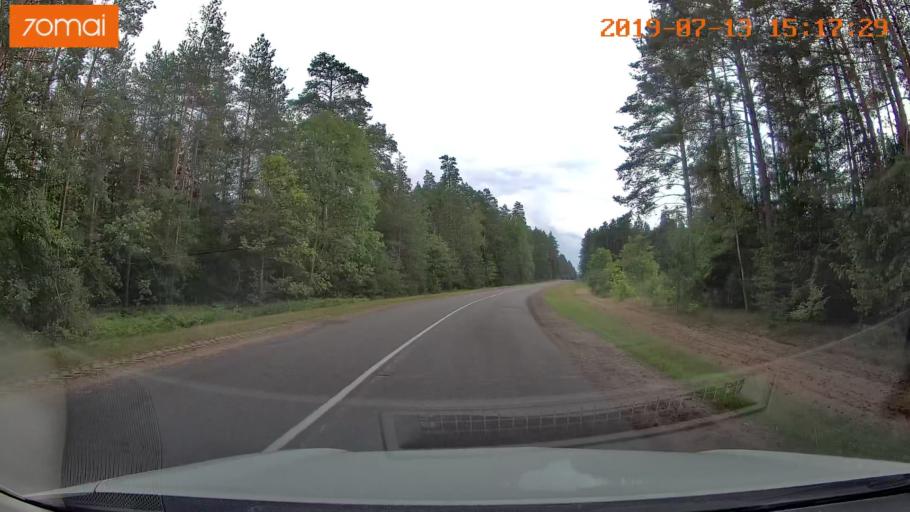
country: BY
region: Mogilev
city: Hlusha
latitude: 53.0954
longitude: 28.8449
